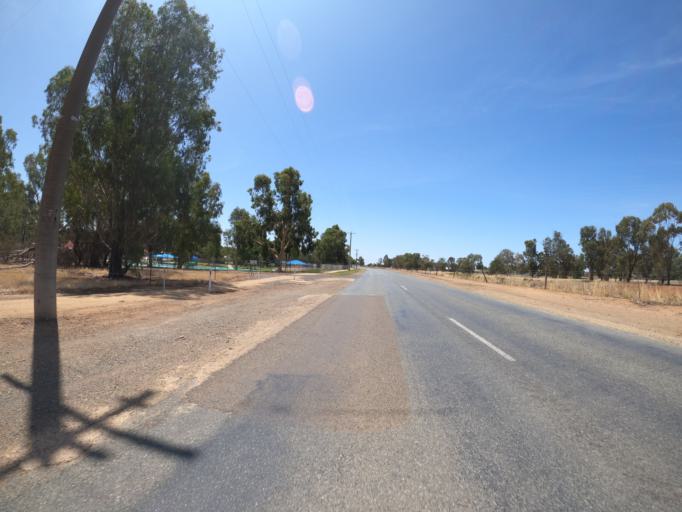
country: AU
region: Victoria
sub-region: Moira
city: Yarrawonga
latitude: -36.0146
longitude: 145.9969
